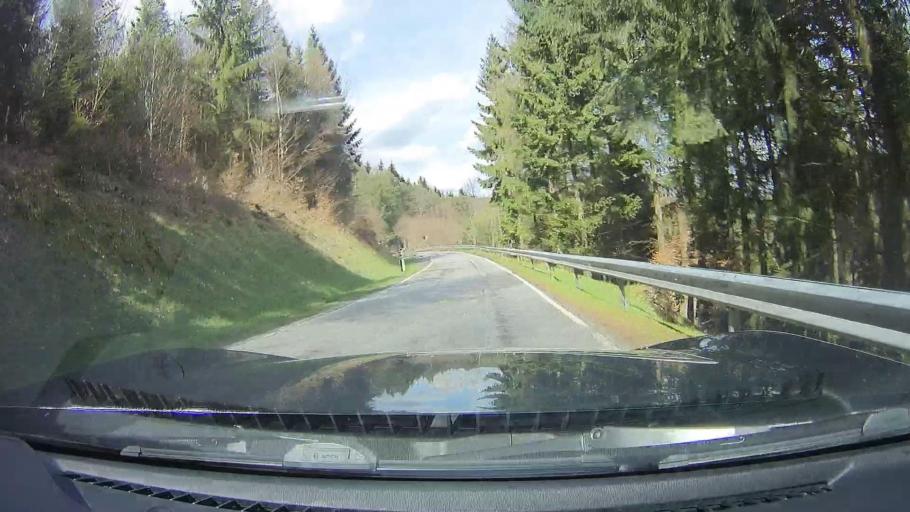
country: DE
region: Hesse
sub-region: Regierungsbezirk Darmstadt
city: Hesseneck
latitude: 49.5593
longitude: 9.1097
